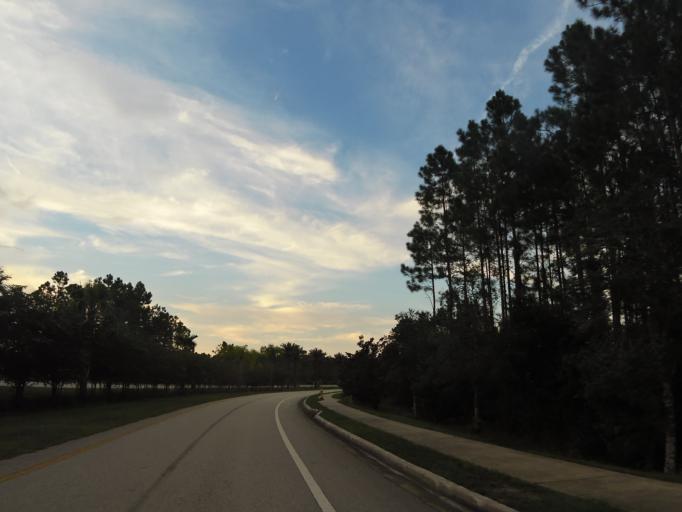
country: US
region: Florida
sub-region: Saint Johns County
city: Fruit Cove
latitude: 30.0810
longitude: -81.6031
